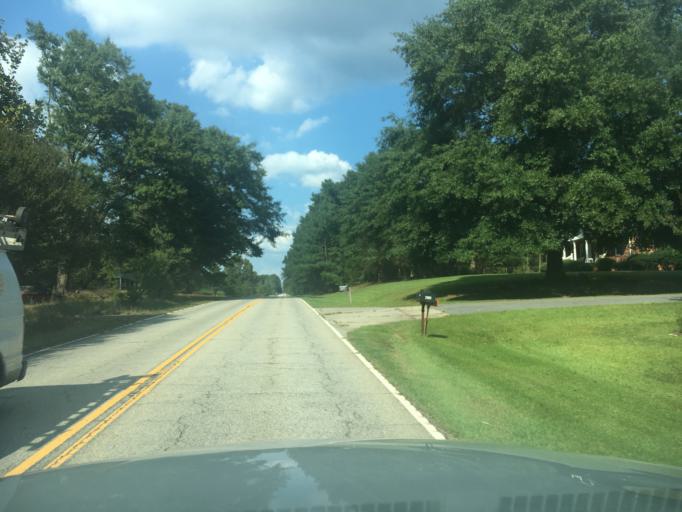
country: US
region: South Carolina
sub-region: Anderson County
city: Pendleton
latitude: 34.6835
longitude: -82.7507
